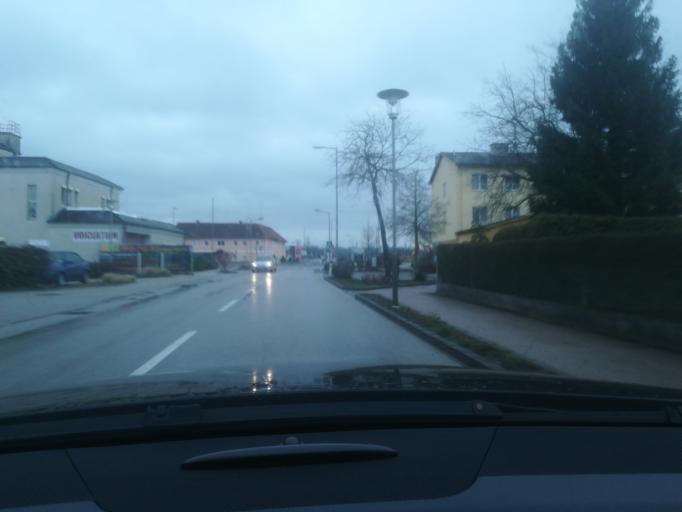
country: AT
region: Upper Austria
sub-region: Wels-Land
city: Marchtrenk
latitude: 48.1923
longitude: 14.1179
